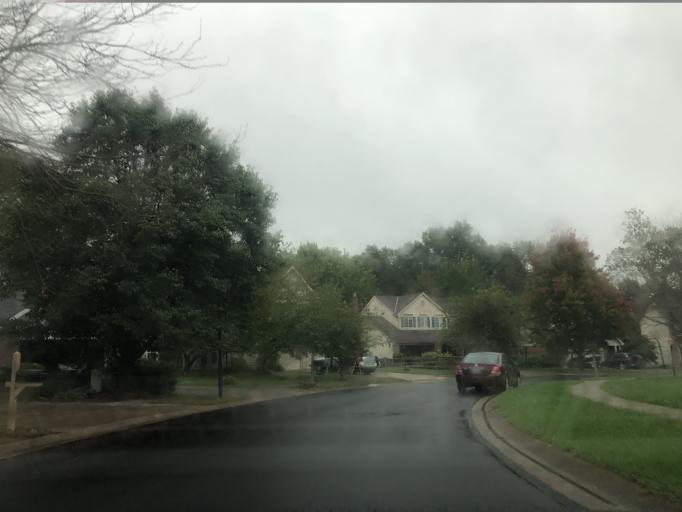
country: US
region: Ohio
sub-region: Hamilton County
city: Loveland
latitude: 39.2650
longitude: -84.2817
